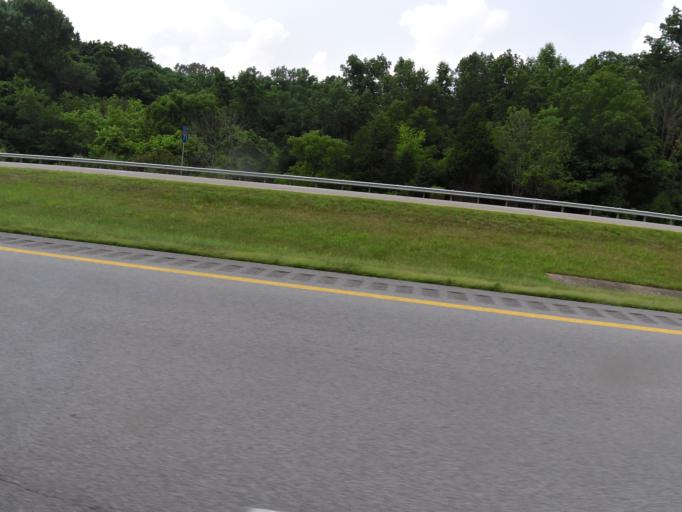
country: US
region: Kentucky
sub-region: Gallatin County
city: Warsaw
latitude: 38.6838
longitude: -84.9579
